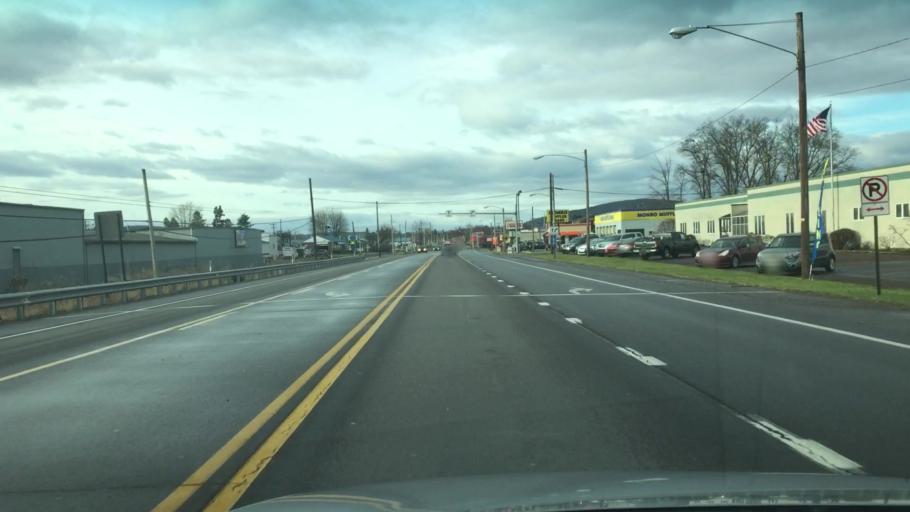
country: US
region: Pennsylvania
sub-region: Columbia County
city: Bloomsburg
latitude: 41.0043
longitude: -76.4381
